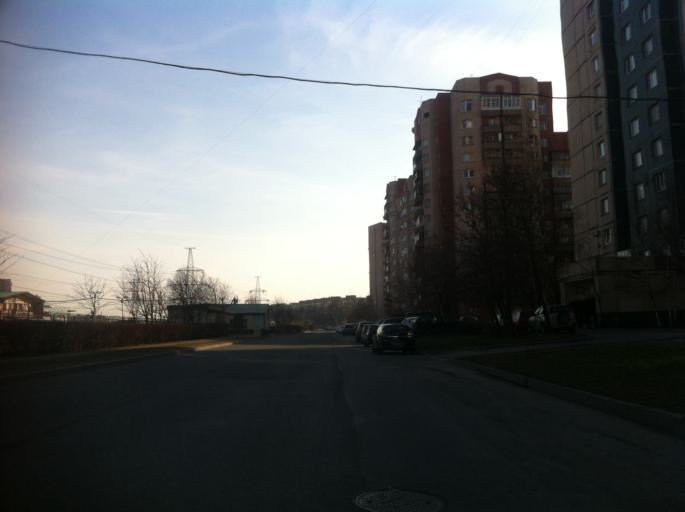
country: RU
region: St.-Petersburg
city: Uritsk
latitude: 59.8550
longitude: 30.1982
